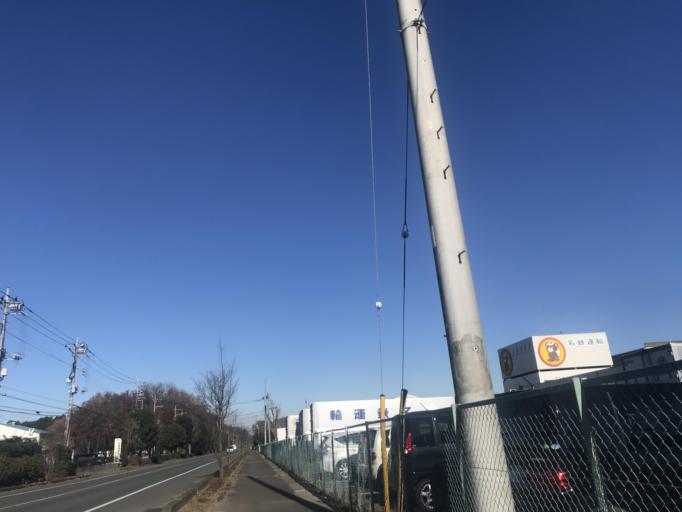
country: JP
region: Ibaraki
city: Yuki
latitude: 36.3314
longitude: 139.8799
